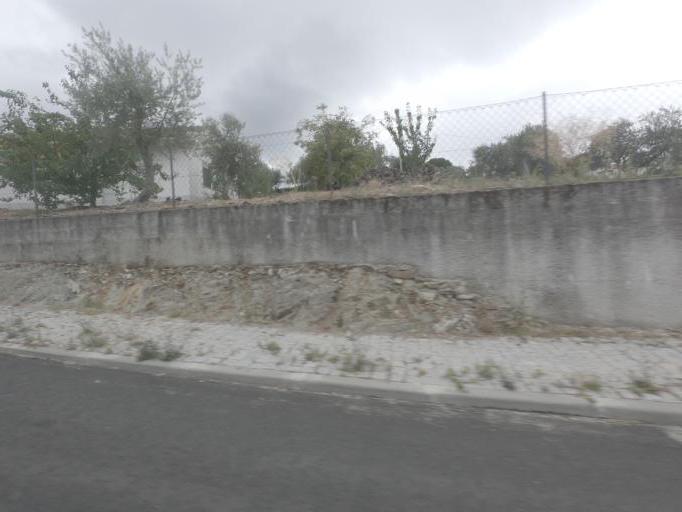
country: PT
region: Vila Real
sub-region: Sabrosa
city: Sabrosa
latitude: 41.2127
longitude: -7.5257
